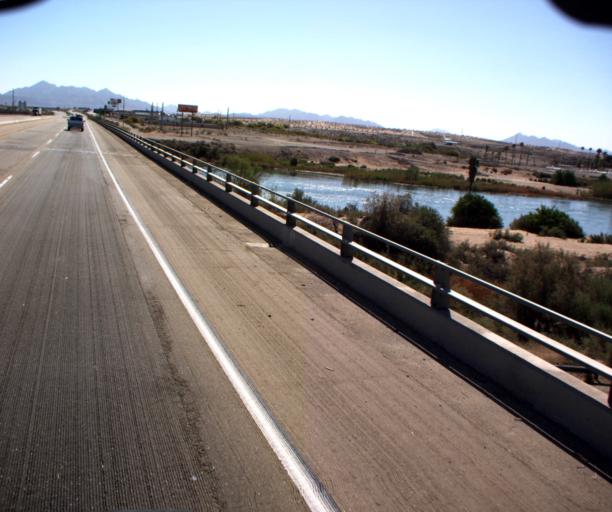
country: US
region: Arizona
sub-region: La Paz County
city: Ehrenberg
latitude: 33.6051
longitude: -114.5327
